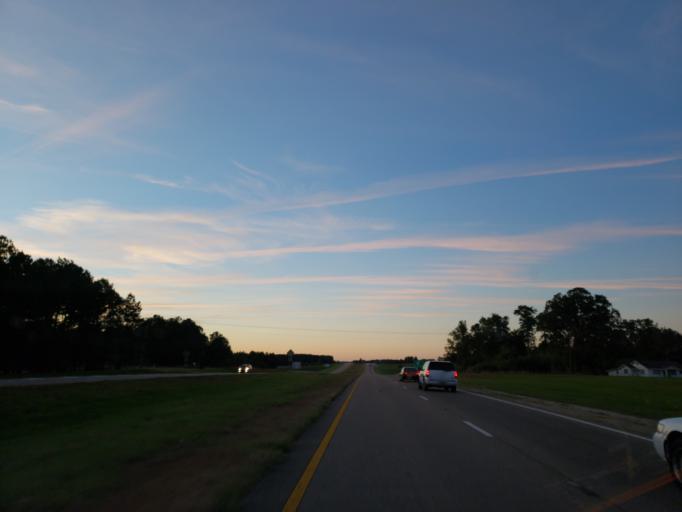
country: US
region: Mississippi
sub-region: Wayne County
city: Waynesboro
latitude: 31.7018
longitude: -88.6215
